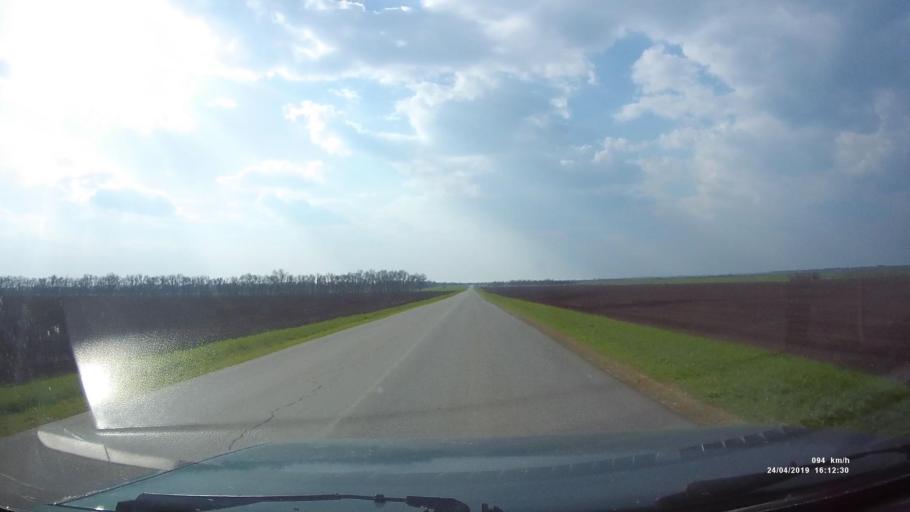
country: RU
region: Rostov
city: Sovetskoye
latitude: 46.7332
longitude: 42.2363
